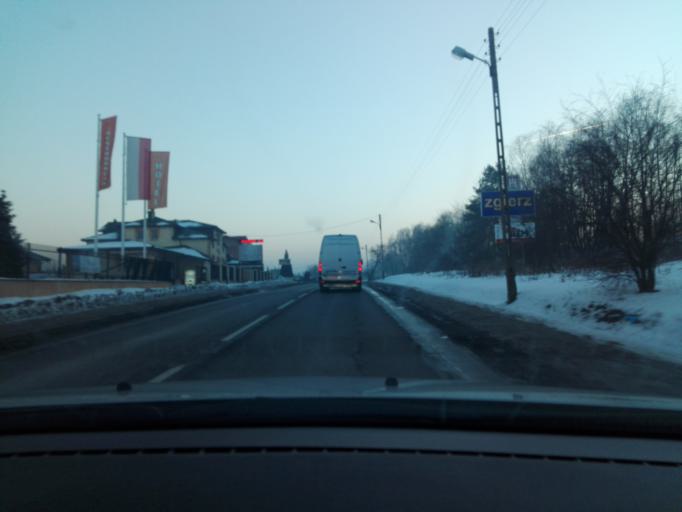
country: PL
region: Lodz Voivodeship
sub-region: Powiat zgierski
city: Zgierz
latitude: 51.8766
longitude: 19.4105
